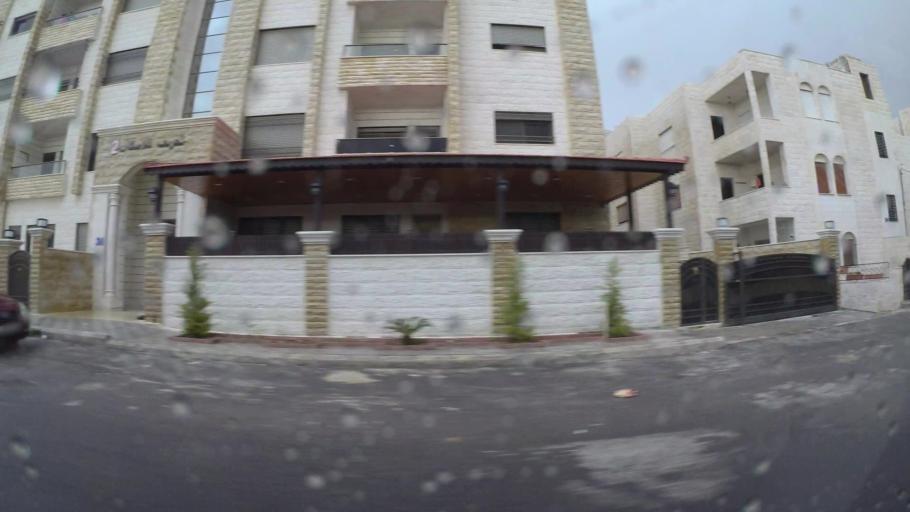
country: JO
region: Amman
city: Amman
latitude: 32.0083
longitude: 35.9564
